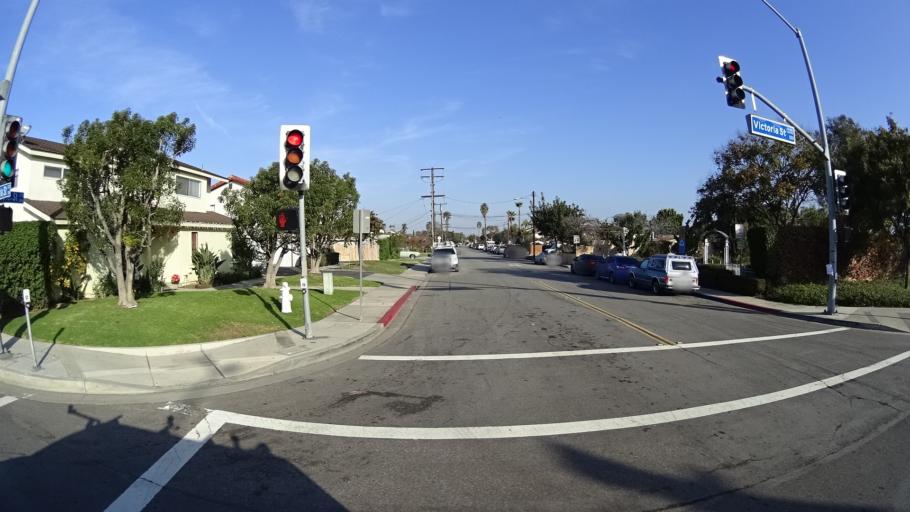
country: US
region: California
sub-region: Orange County
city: Costa Mesa
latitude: 33.6526
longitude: -117.9227
